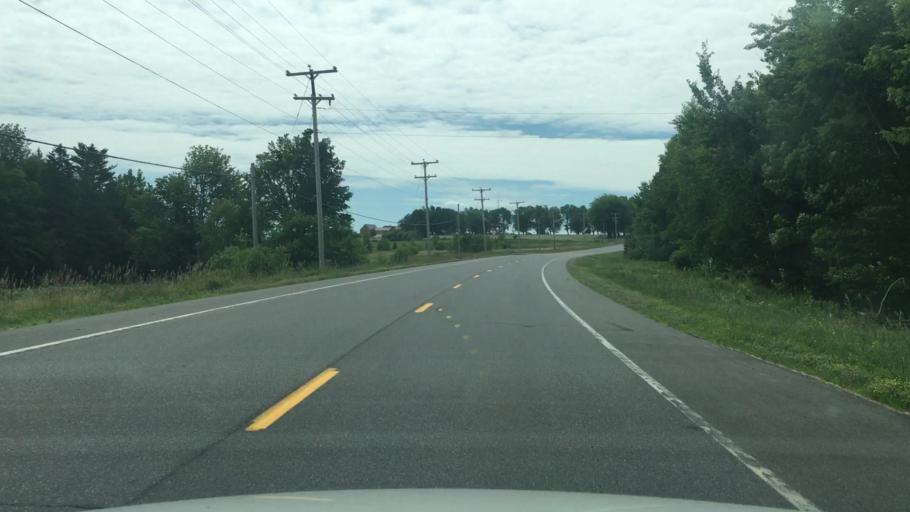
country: US
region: Maine
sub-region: Waldo County
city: Troy
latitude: 44.5468
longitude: -69.2659
